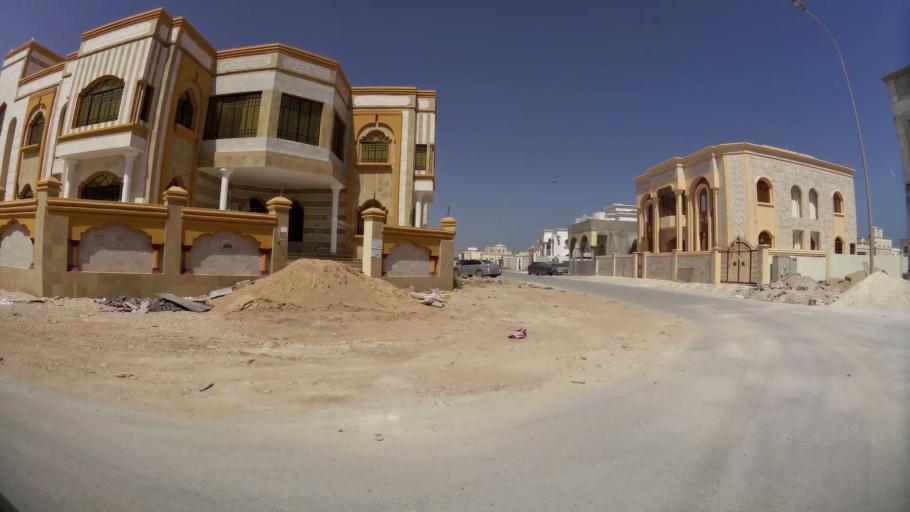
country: OM
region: Zufar
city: Salalah
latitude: 17.0410
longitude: 54.1556
